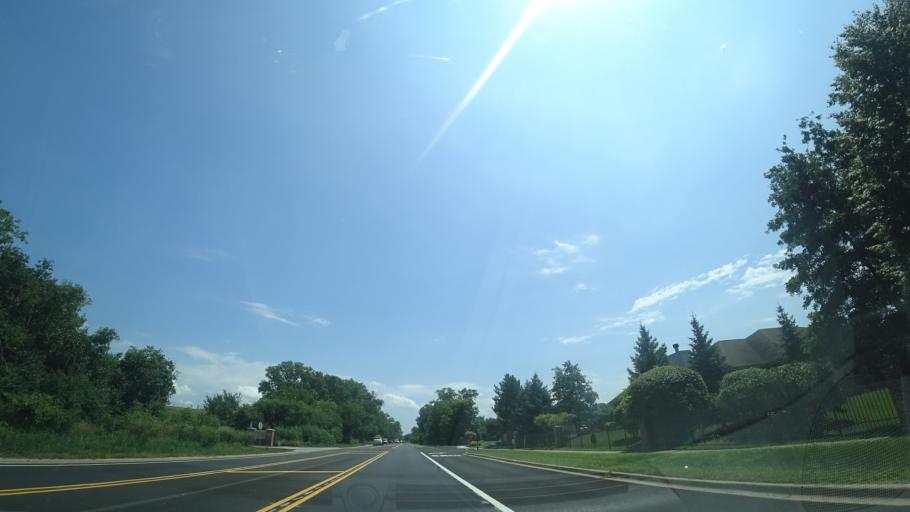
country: US
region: Illinois
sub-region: Cook County
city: Crestwood
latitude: 41.6696
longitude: -87.7717
